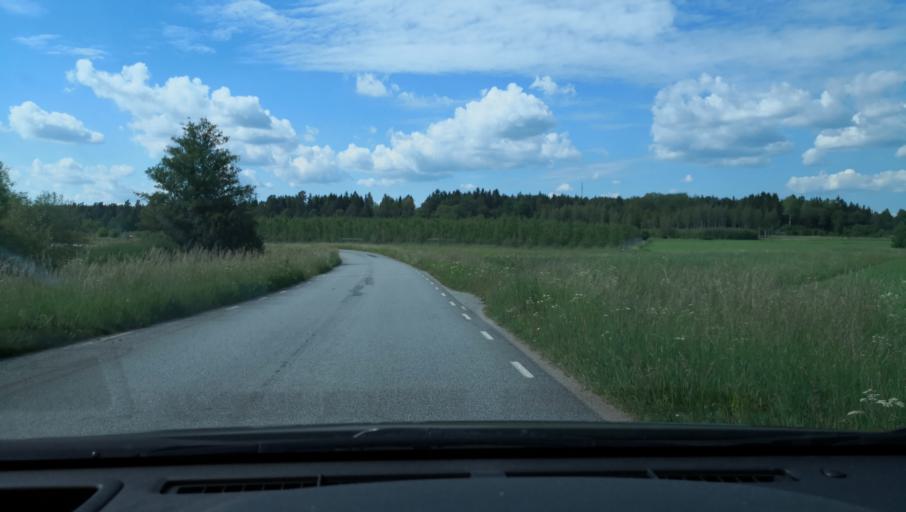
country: SE
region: Uppsala
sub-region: Enkopings Kommun
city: Orsundsbro
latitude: 59.8154
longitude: 17.3692
